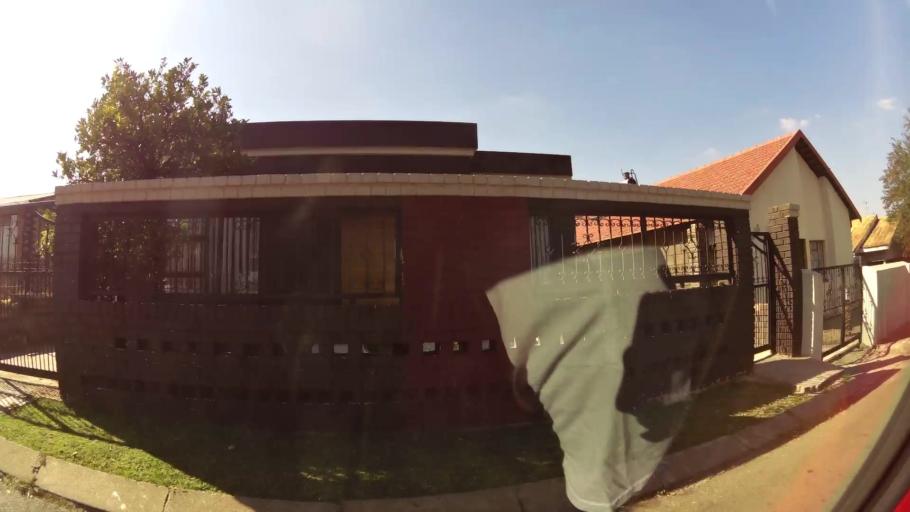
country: ZA
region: Gauteng
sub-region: City of Johannesburg Metropolitan Municipality
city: Soweto
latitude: -26.2446
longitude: 27.9006
